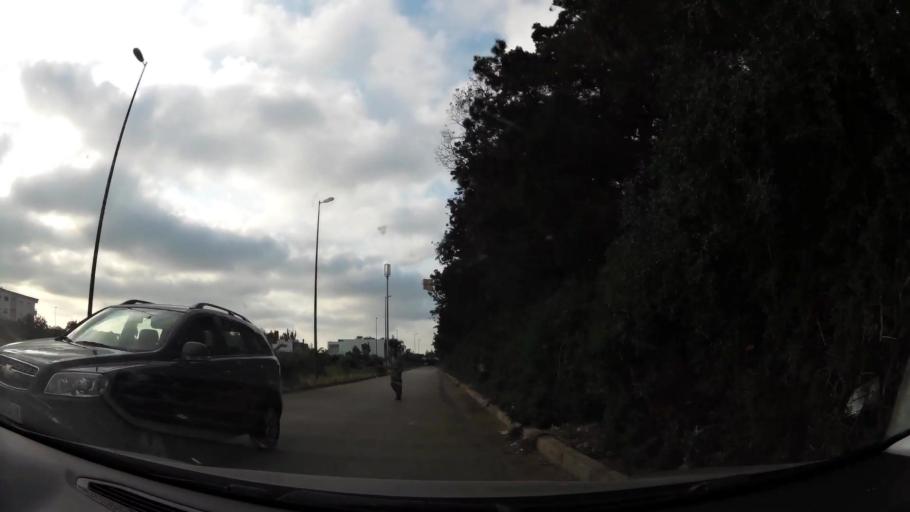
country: MA
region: Rabat-Sale-Zemmour-Zaer
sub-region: Rabat
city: Rabat
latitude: 33.9492
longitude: -6.8426
